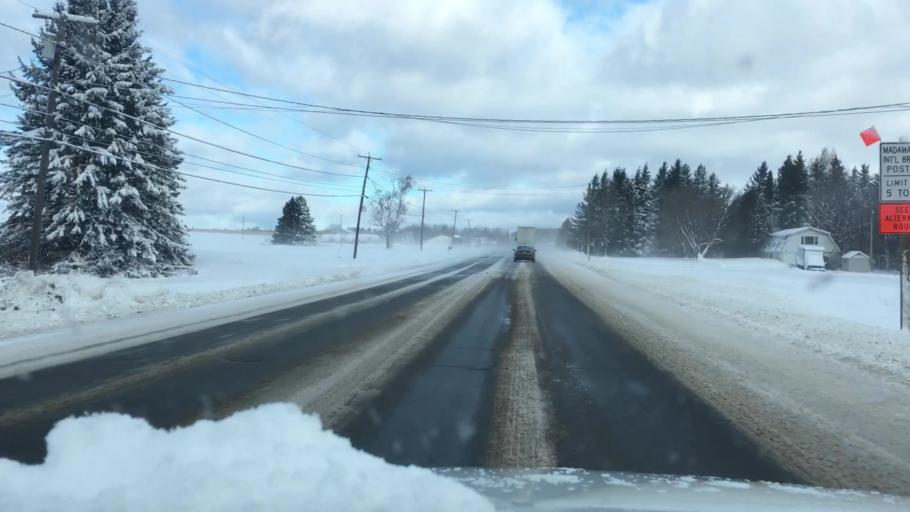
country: US
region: Maine
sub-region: Aroostook County
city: Caribou
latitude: 46.8068
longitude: -67.9941
